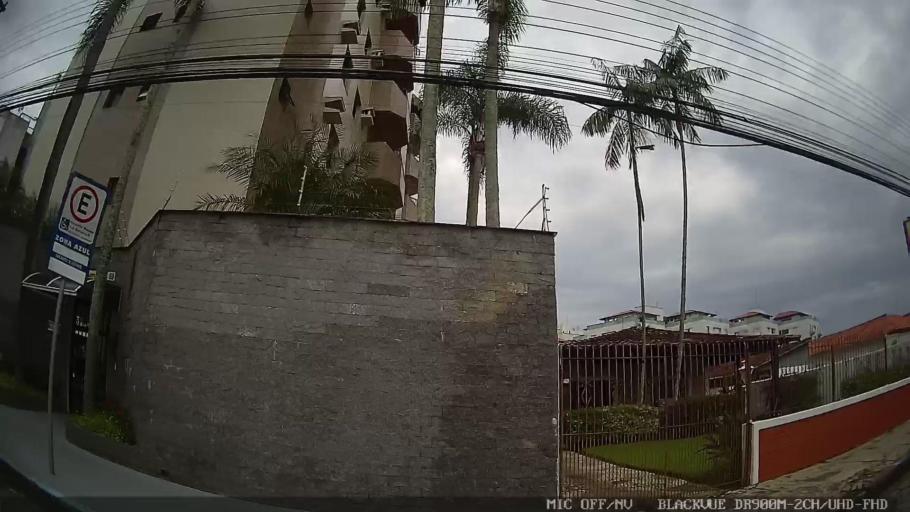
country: BR
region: Sao Paulo
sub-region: Caraguatatuba
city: Caraguatatuba
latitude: -23.6243
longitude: -45.4141
